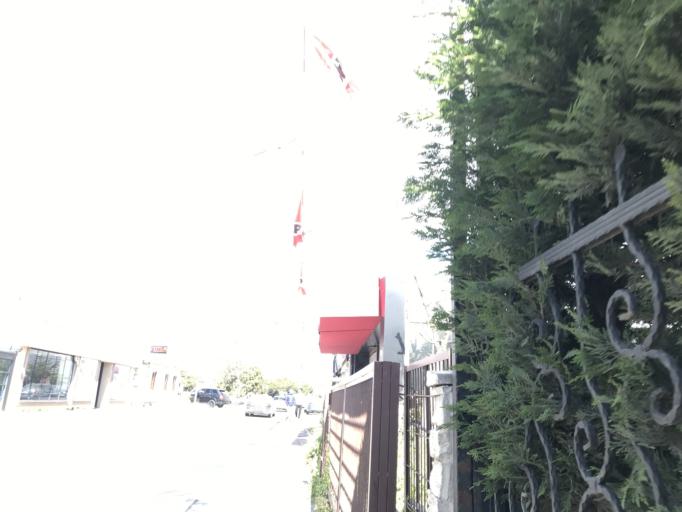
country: TR
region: Istanbul
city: Maltepe
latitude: 40.9250
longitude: 29.1252
